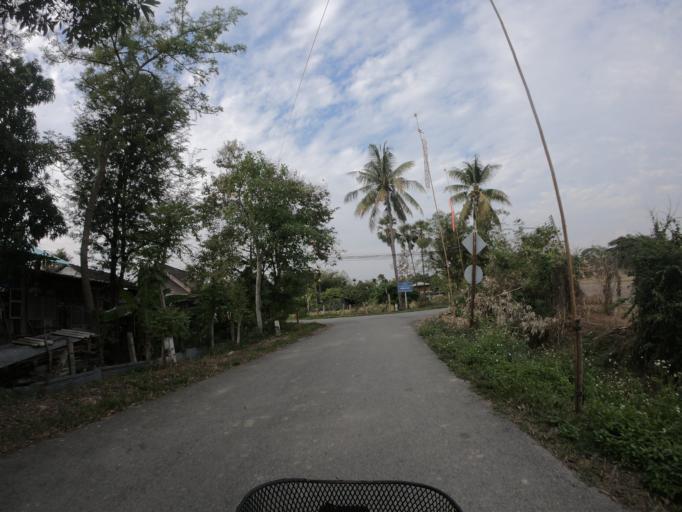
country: TH
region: Chiang Mai
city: San Sai
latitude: 18.7991
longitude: 99.0522
